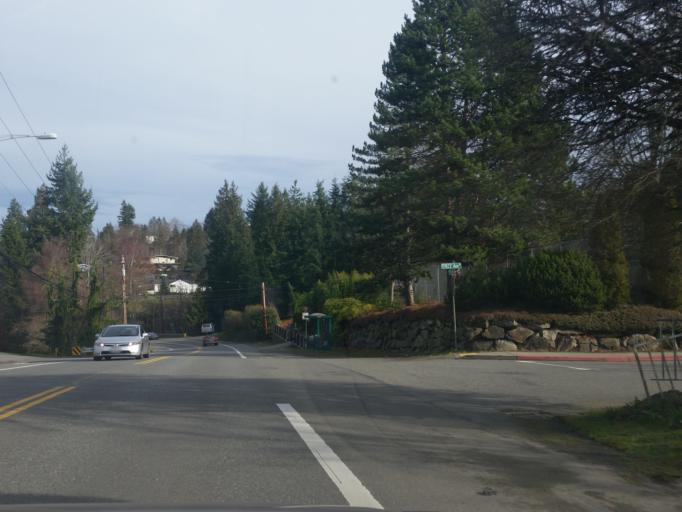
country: US
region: Washington
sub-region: Snohomish County
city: Mukilteo
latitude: 47.9535
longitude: -122.2643
